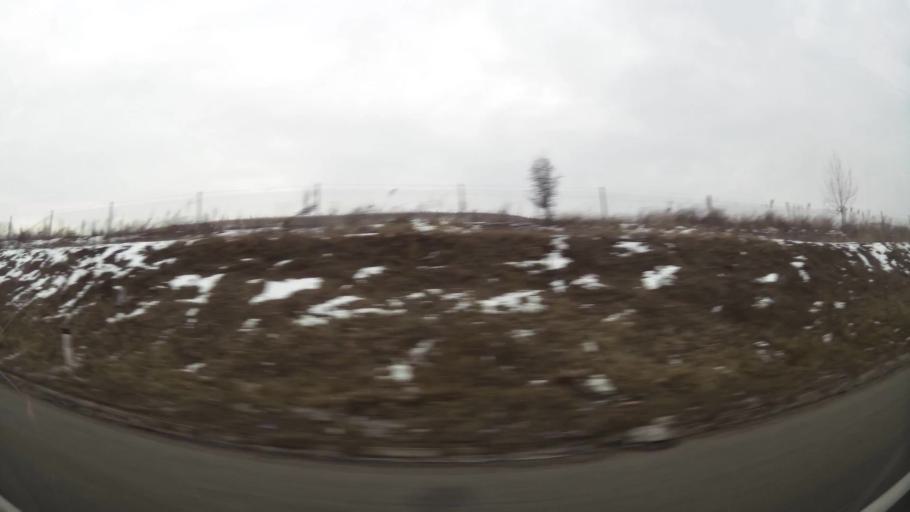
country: MK
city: Kondovo
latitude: 42.0248
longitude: 21.3301
